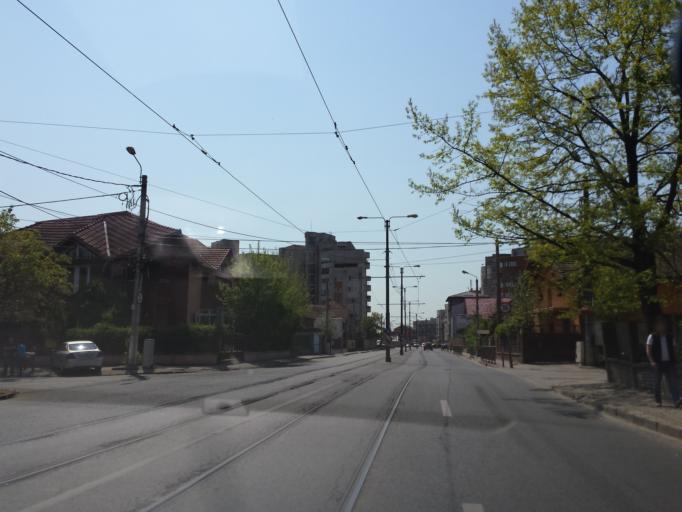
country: RO
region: Timis
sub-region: Comuna Dumbravita
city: Dumbravita
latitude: 45.7676
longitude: 21.2605
